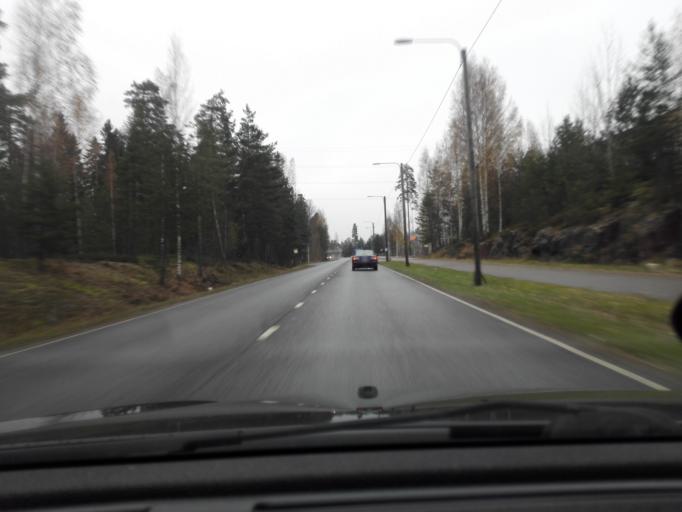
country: FI
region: Uusimaa
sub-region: Helsinki
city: Vantaa
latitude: 60.3030
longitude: 25.0913
